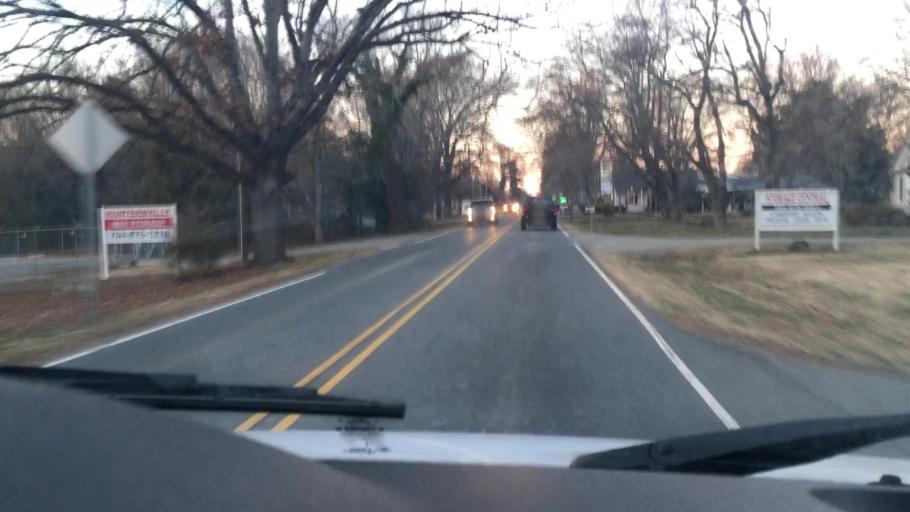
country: US
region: North Carolina
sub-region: Mecklenburg County
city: Huntersville
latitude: 35.4280
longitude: -80.8429
